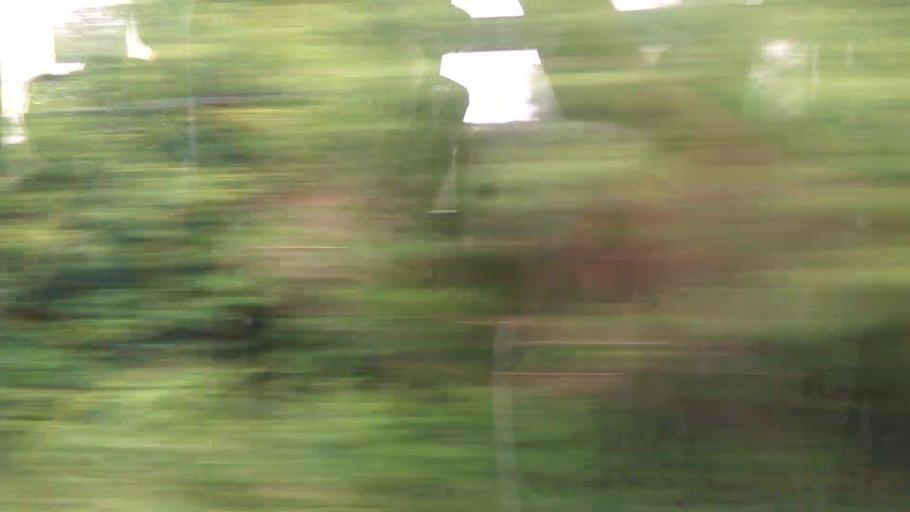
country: RU
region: Moskovskaya
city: Lukhovitsy
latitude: 54.9274
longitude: 39.0016
